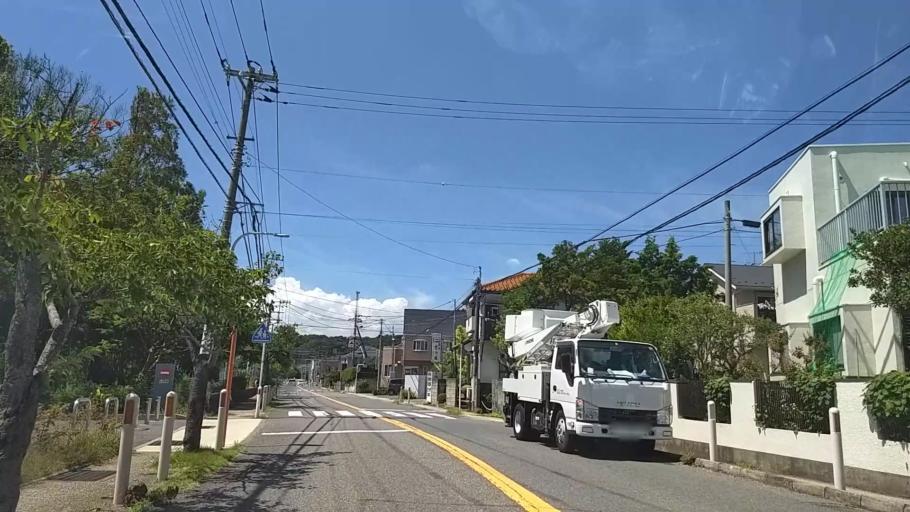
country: JP
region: Kanagawa
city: Zushi
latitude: 35.3012
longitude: 139.5934
